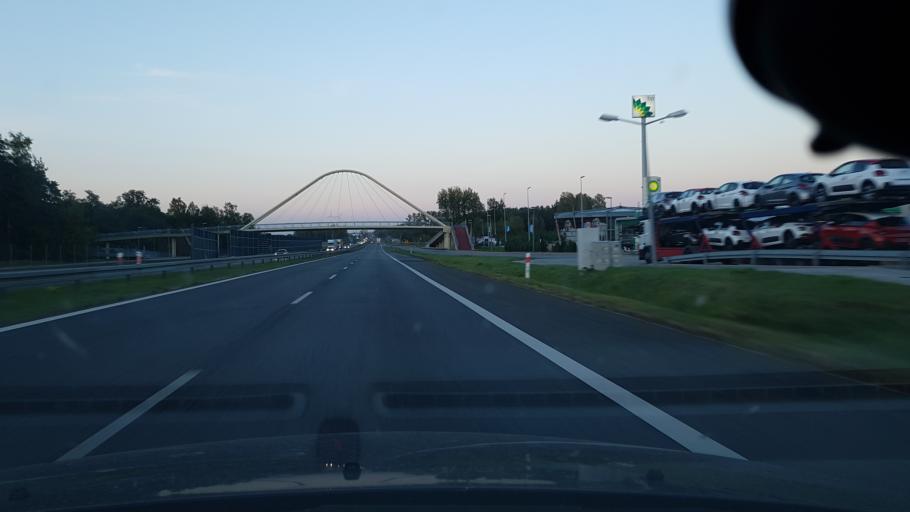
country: PL
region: Masovian Voivodeship
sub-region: Powiat zyrardowski
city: Mszczonow
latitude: 51.9507
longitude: 20.4905
